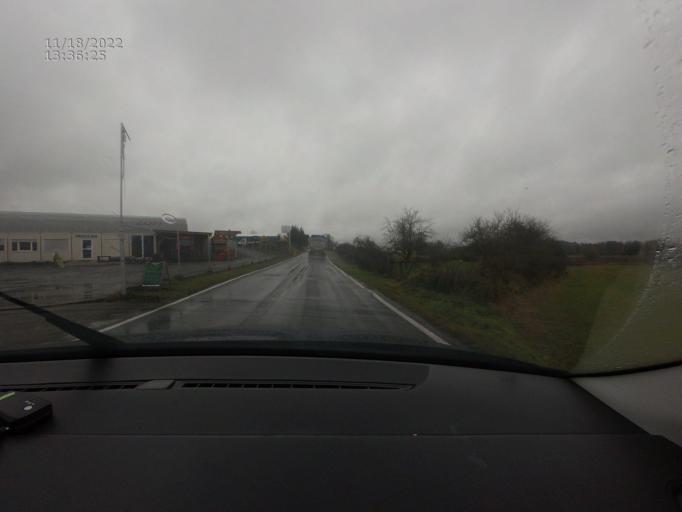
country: CZ
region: Plzensky
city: Kasejovice
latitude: 49.4138
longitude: 13.7821
